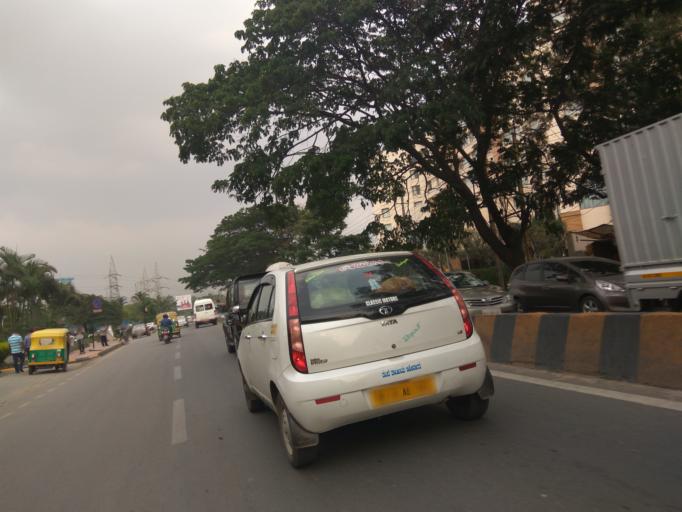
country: IN
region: Karnataka
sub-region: Bangalore Urban
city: Bangalore
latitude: 12.9778
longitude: 77.7140
